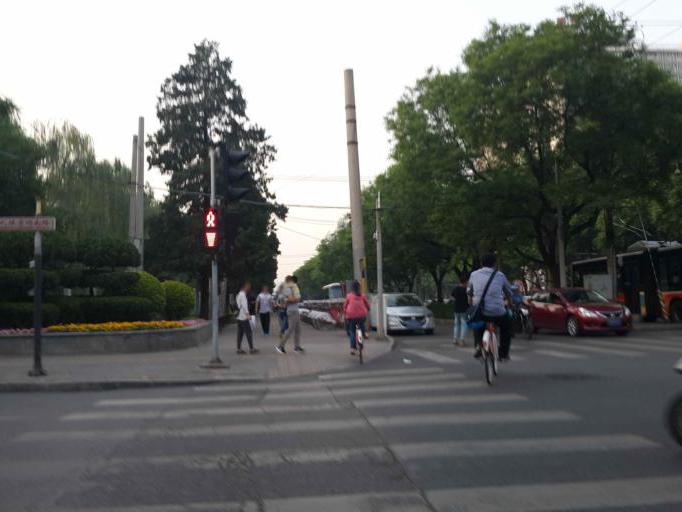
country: CN
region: Beijing
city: Chaowai
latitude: 39.9256
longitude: 116.4438
